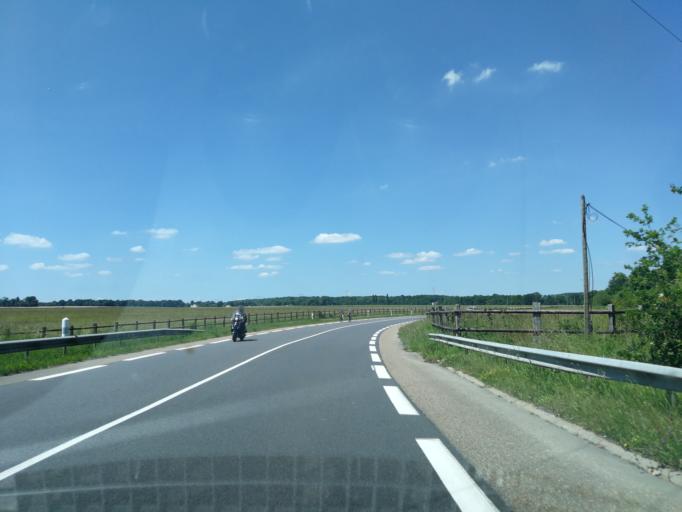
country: FR
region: Ile-de-France
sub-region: Departement de l'Essonne
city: Briis-sous-Forges
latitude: 48.6170
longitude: 2.1180
